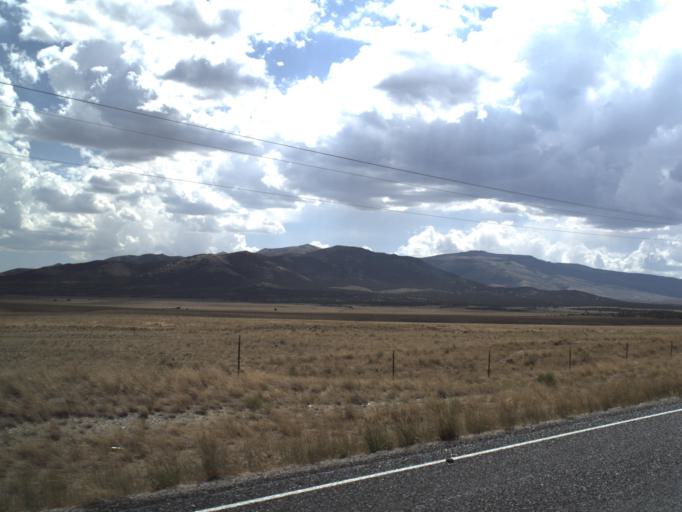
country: US
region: Idaho
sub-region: Minidoka County
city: Rupert
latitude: 41.9703
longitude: -113.1241
